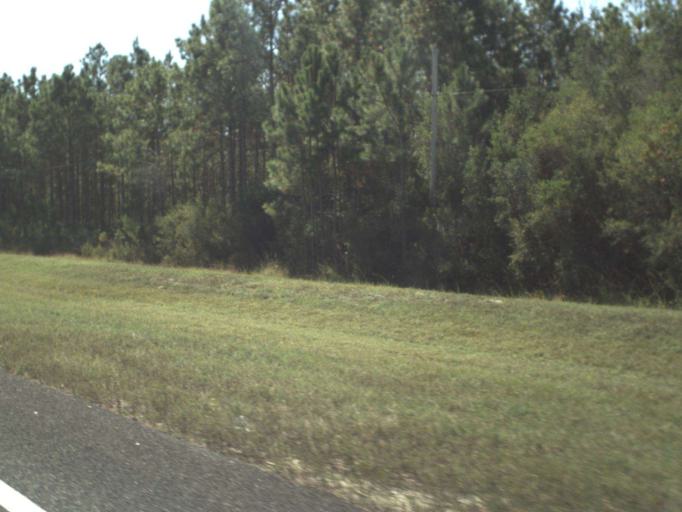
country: US
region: Florida
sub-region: Walton County
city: Seaside
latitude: 30.3187
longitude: -86.0448
